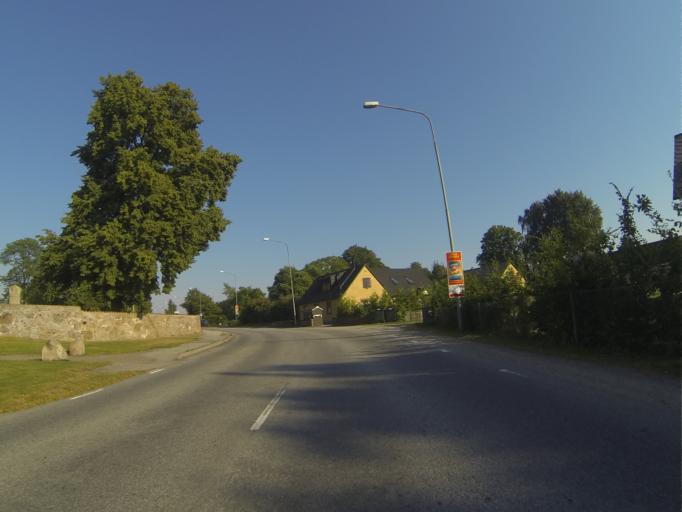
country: SE
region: Skane
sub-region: Lunds Kommun
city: Genarp
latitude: 55.6030
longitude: 13.3954
